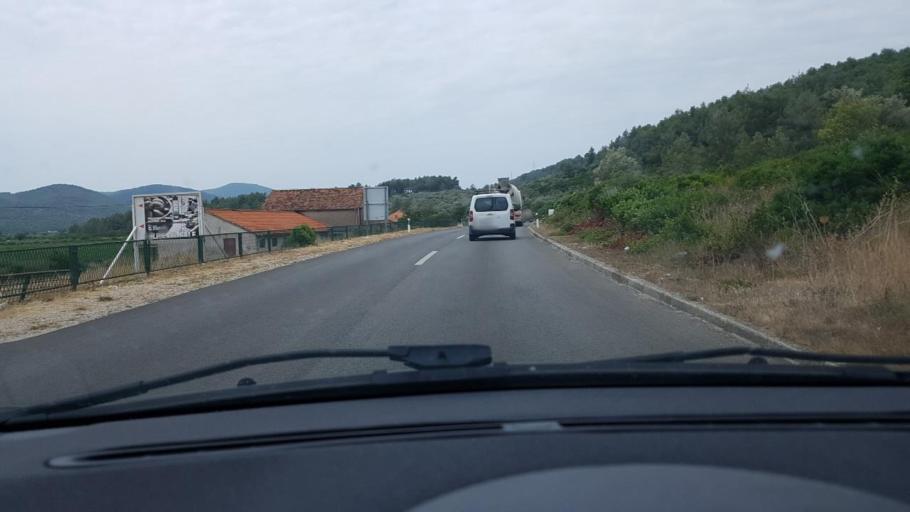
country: HR
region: Dubrovacko-Neretvanska
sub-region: Grad Dubrovnik
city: Vela Luka
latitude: 42.9477
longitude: 16.7739
